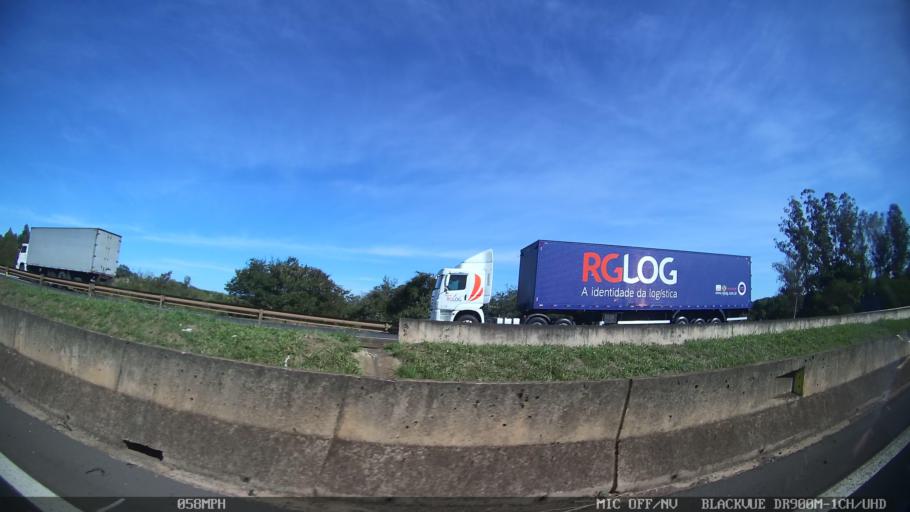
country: BR
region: Sao Paulo
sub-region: Leme
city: Leme
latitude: -22.0994
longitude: -47.4155
